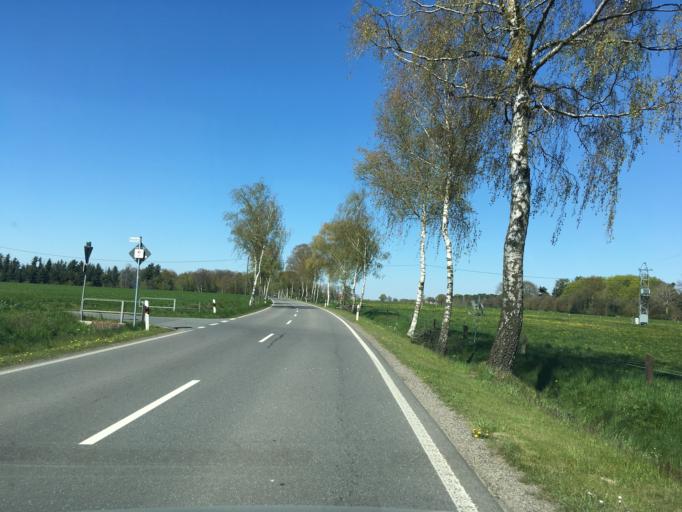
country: DE
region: North Rhine-Westphalia
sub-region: Regierungsbezirk Munster
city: Borken
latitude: 51.8576
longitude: 6.7897
